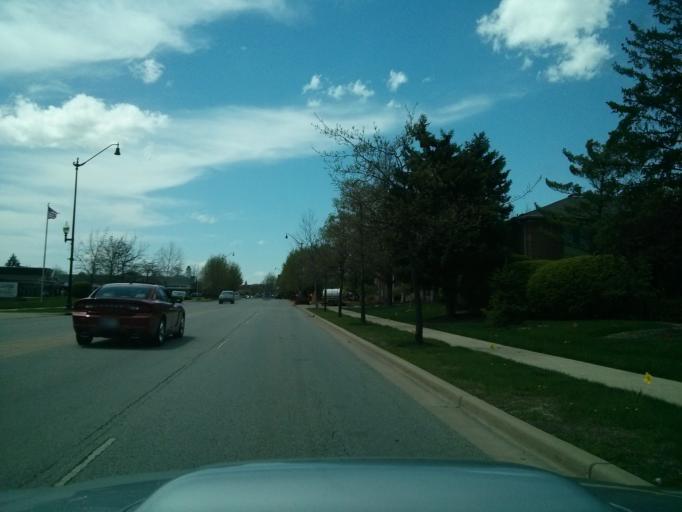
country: US
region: Indiana
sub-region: Hamilton County
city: Carmel
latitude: 39.9621
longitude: -86.1190
